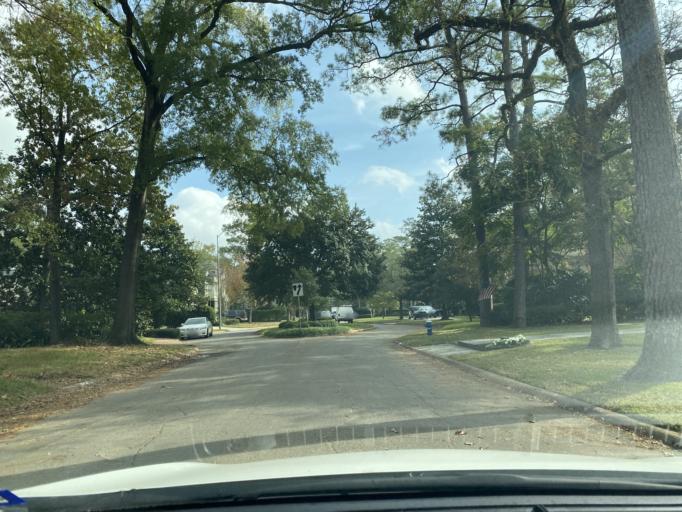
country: US
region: Texas
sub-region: Harris County
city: Hunters Creek Village
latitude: 29.7644
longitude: -95.4696
